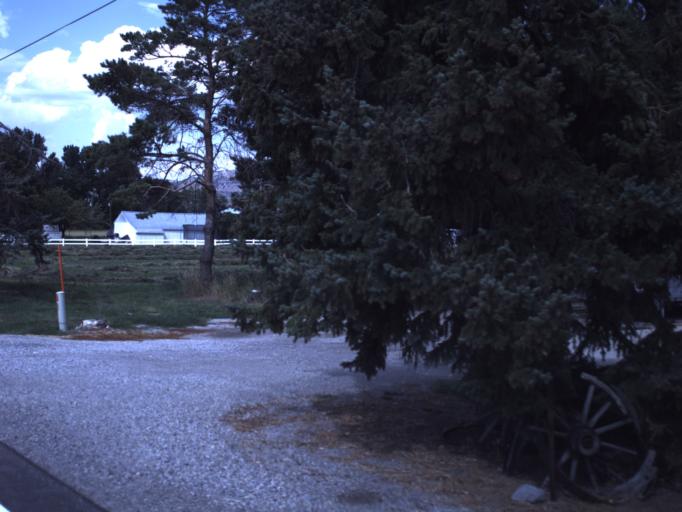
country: US
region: Utah
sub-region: Box Elder County
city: Garland
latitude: 41.8048
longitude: -112.1159
